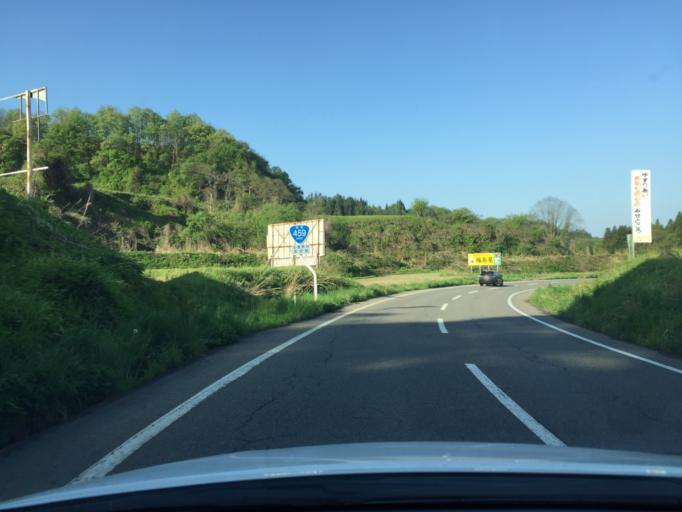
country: JP
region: Fukushima
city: Kitakata
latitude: 37.6624
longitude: 139.9616
